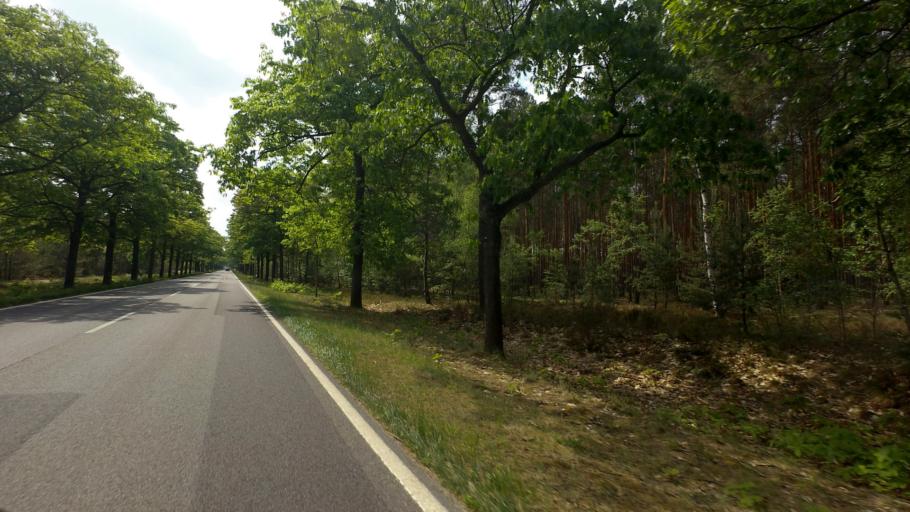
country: DE
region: Brandenburg
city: Drachhausen
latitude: 51.9287
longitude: 14.3457
